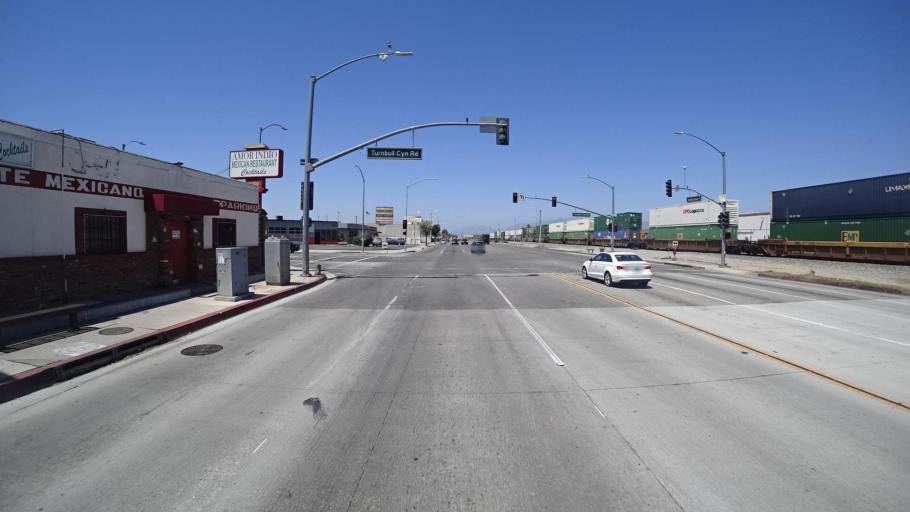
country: US
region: California
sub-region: Los Angeles County
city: La Puente
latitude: 34.0272
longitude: -117.9643
